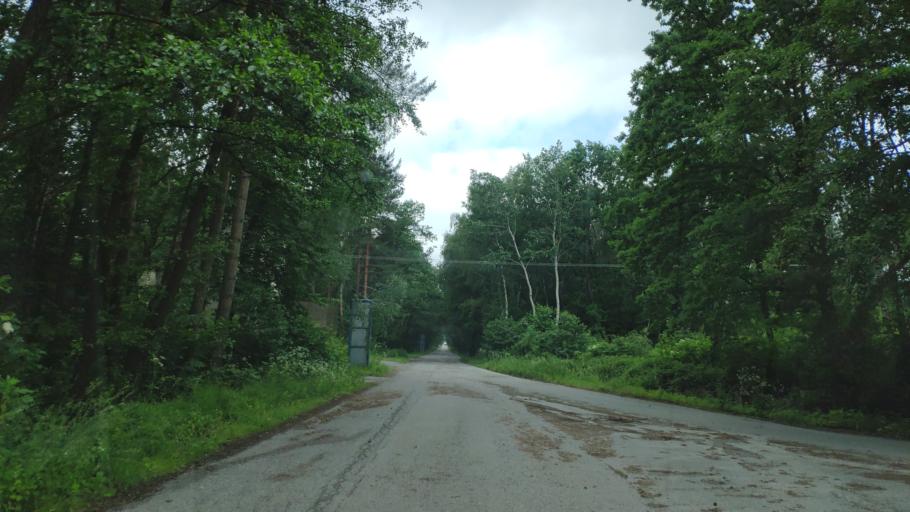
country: SK
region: Presovsky
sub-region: Okres Presov
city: Presov
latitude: 48.9998
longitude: 21.3206
